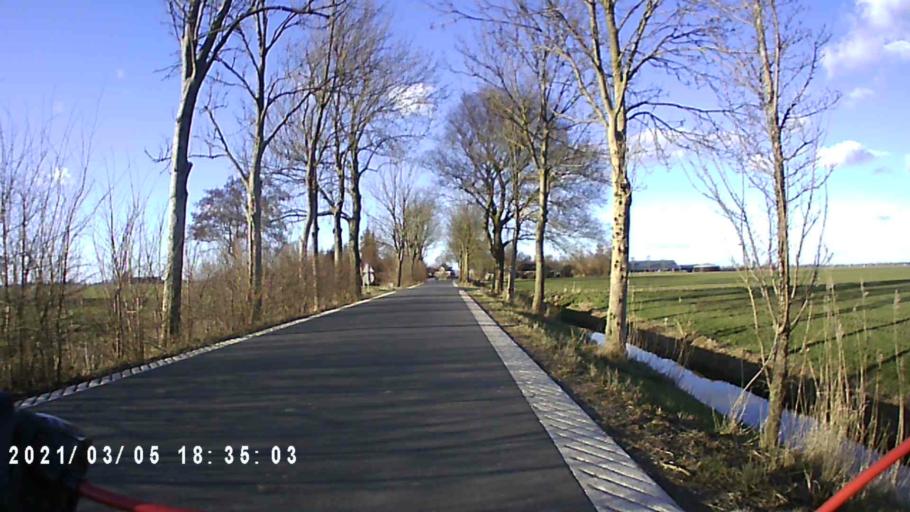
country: NL
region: Groningen
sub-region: Gemeente Groningen
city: Korrewegwijk
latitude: 53.2678
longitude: 6.5654
